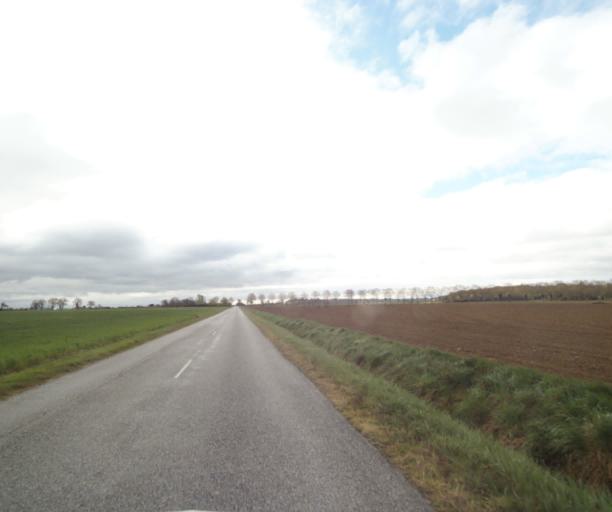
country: FR
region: Midi-Pyrenees
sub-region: Departement de l'Ariege
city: Saverdun
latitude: 43.2536
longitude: 1.5446
